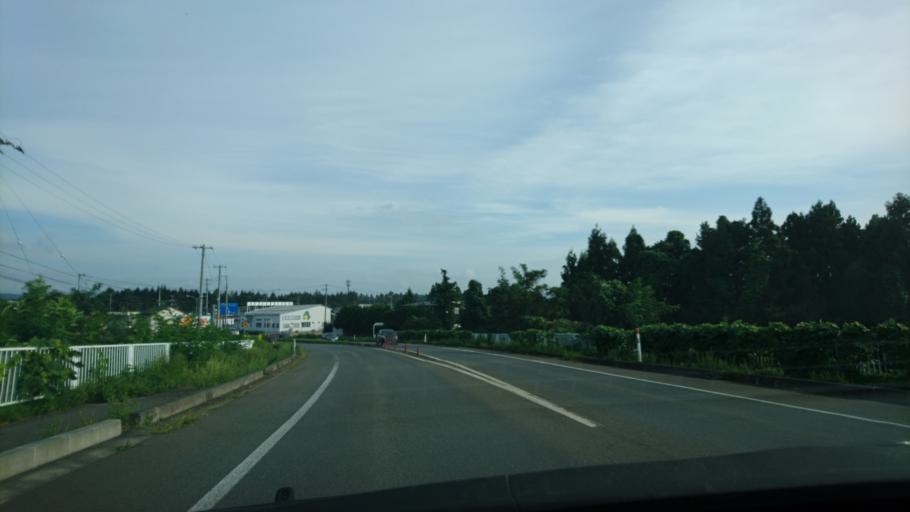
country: JP
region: Iwate
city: Kitakami
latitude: 39.2965
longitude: 141.0835
